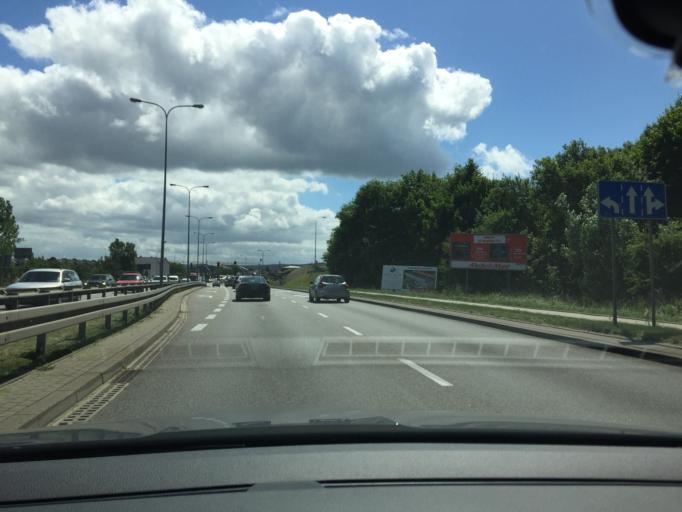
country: PL
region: Pomeranian Voivodeship
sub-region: Powiat wejherowski
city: Reda
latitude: 54.5910
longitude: 18.3572
